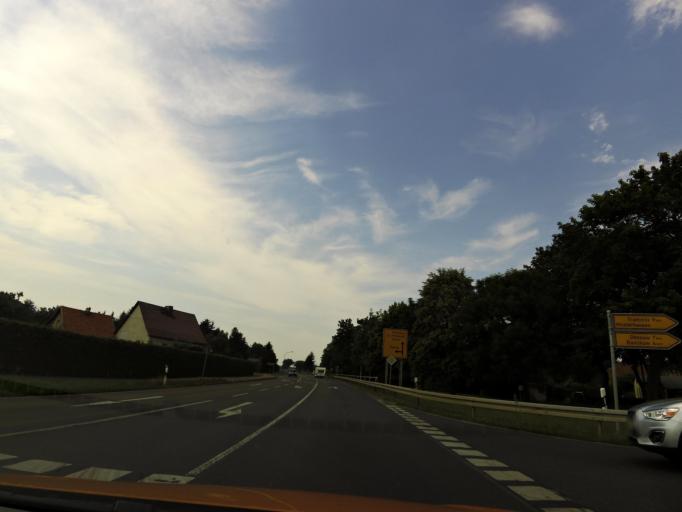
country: DE
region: Brandenburg
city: Wusterhausen
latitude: 52.8970
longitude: 12.4530
